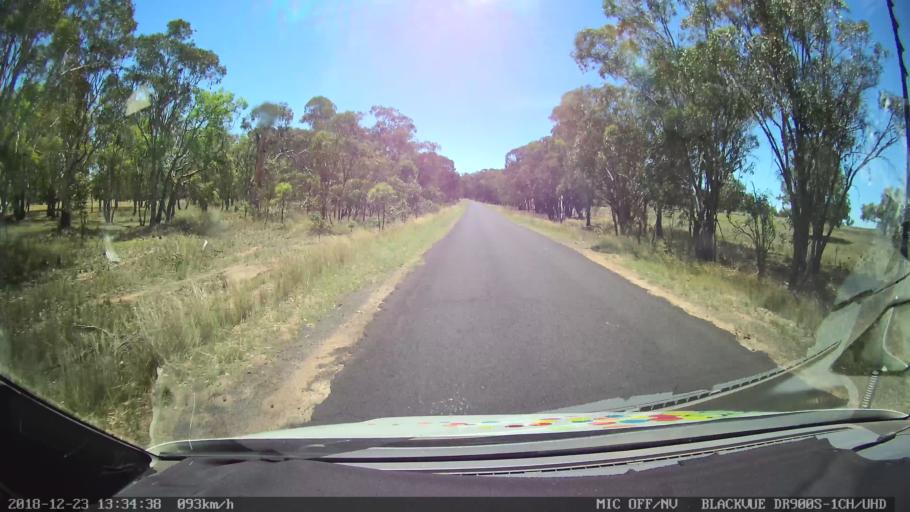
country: AU
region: New South Wales
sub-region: Armidale Dumaresq
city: Armidale
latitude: -30.4471
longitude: 151.2634
